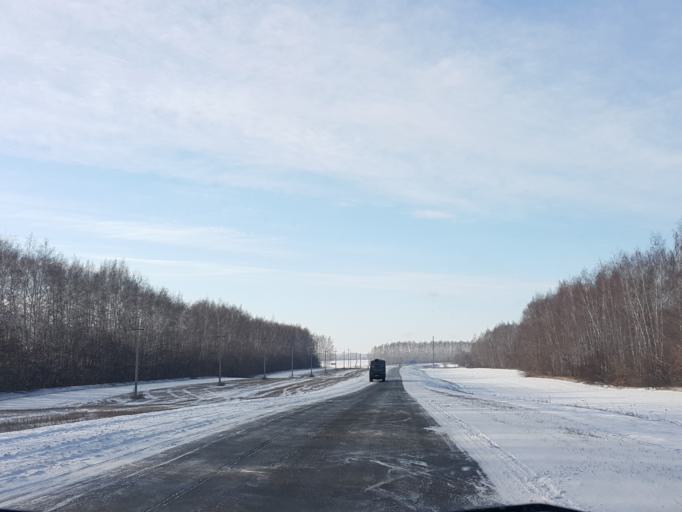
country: RU
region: Tambov
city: Znamenka
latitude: 52.3757
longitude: 41.3068
